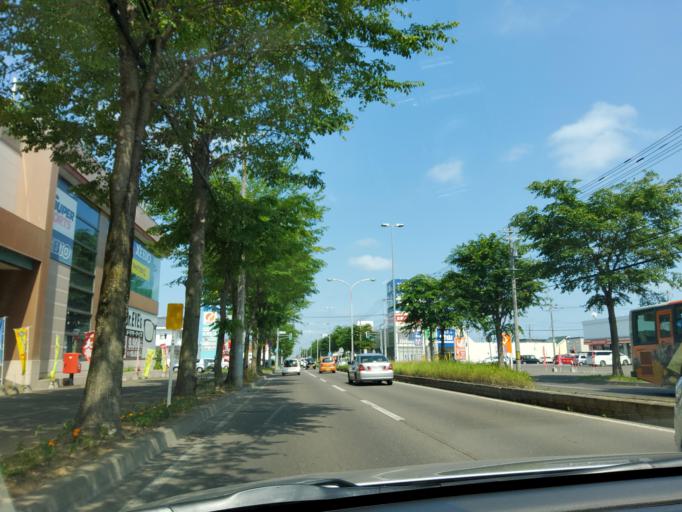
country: JP
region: Hokkaido
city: Obihiro
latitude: 42.9183
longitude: 143.1517
